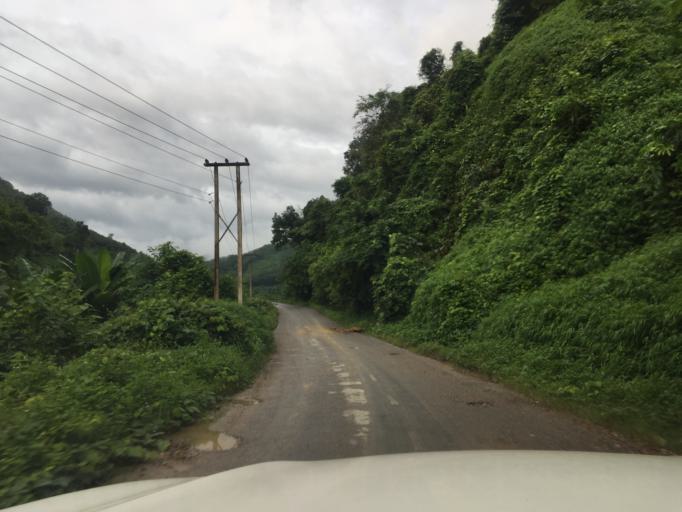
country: LA
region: Oudomxai
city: Muang La
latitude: 21.0290
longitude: 102.2364
